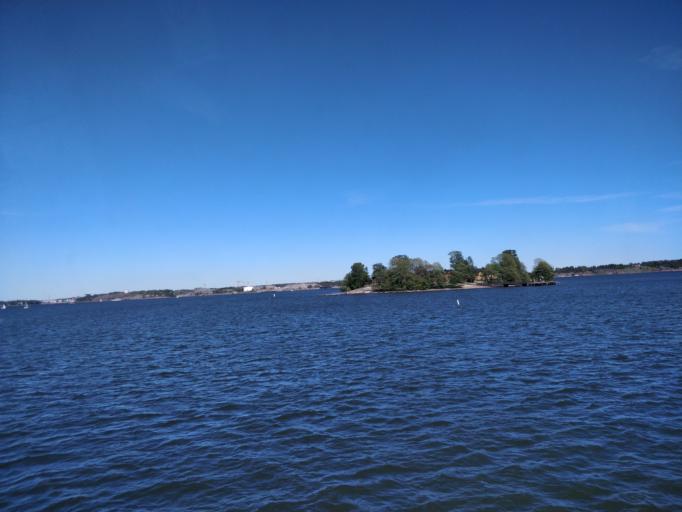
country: FI
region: Uusimaa
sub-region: Helsinki
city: Helsinki
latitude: 60.1532
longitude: 24.9833
